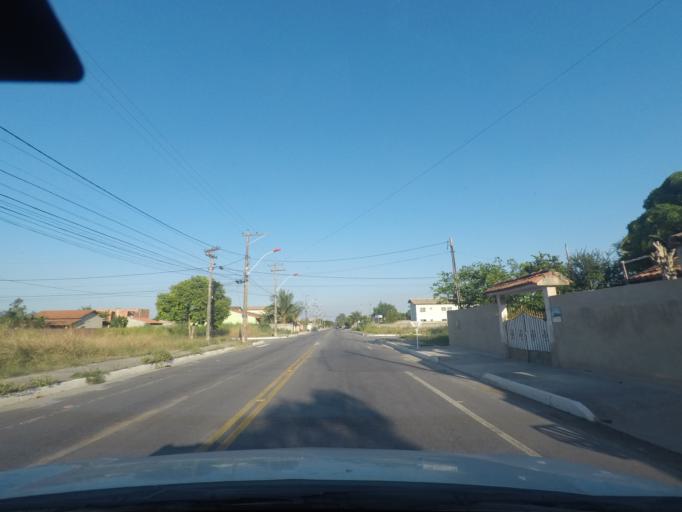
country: BR
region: Rio de Janeiro
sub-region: Marica
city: Marica
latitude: -22.9566
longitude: -42.9347
